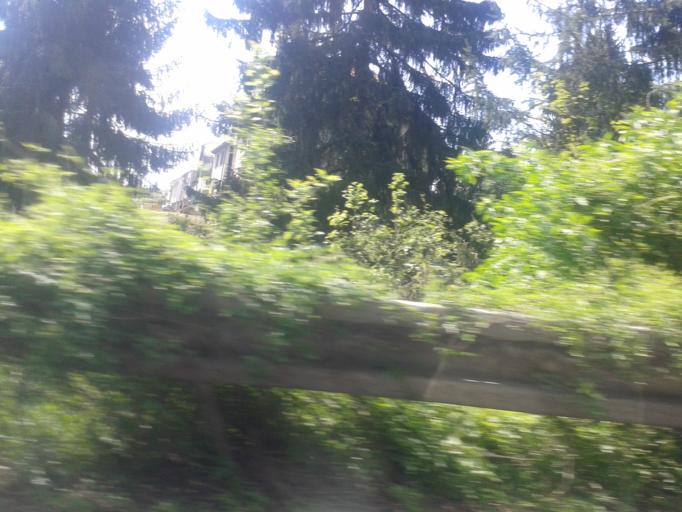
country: CZ
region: Central Bohemia
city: Zdice
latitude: 49.9168
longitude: 13.9840
